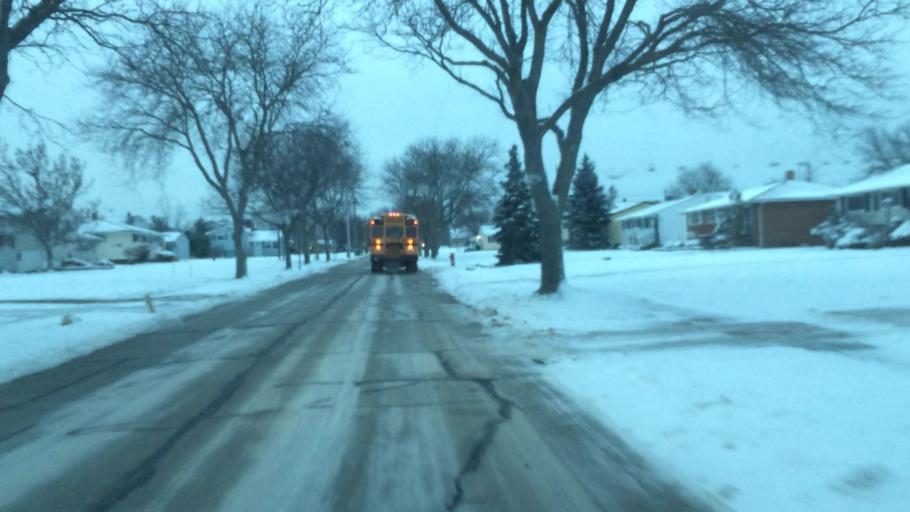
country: US
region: Ohio
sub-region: Cuyahoga County
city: Oakwood
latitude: 41.3749
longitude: -81.5003
